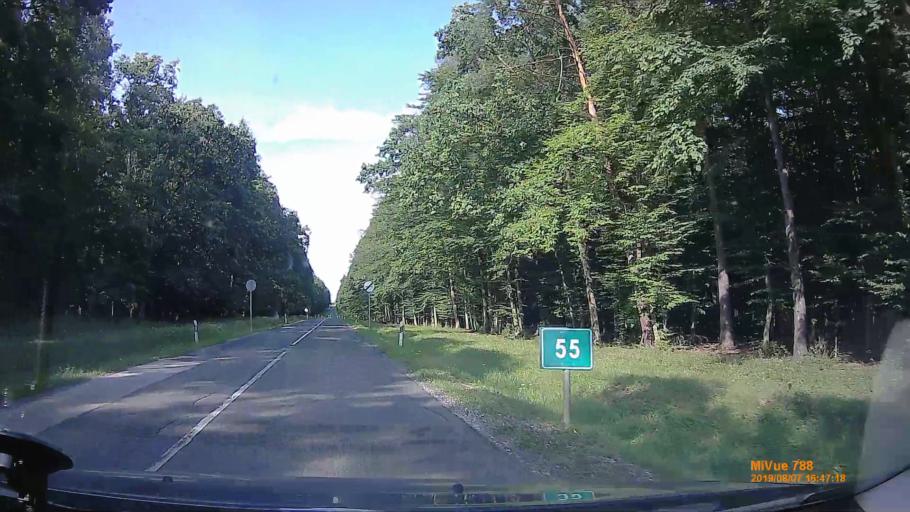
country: HU
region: Zala
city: Lenti
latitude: 46.6607
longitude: 16.6338
